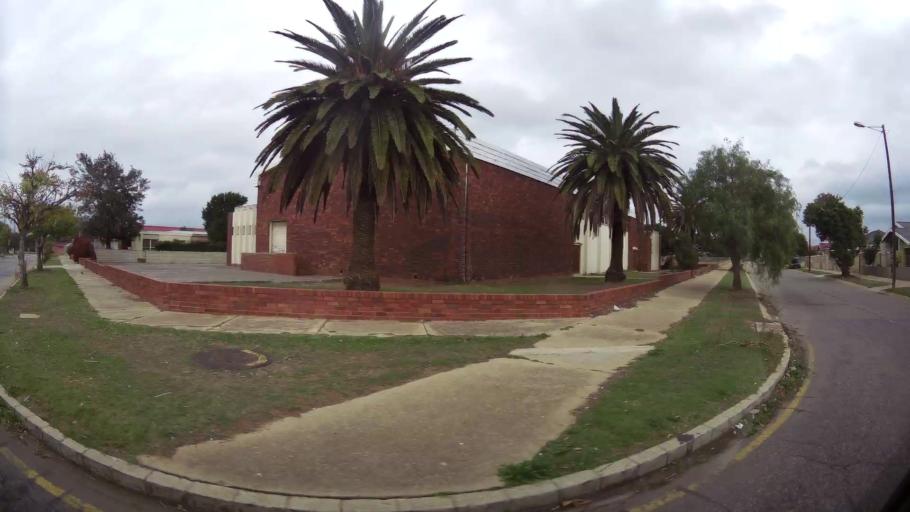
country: ZA
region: Eastern Cape
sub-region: Nelson Mandela Bay Metropolitan Municipality
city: Port Elizabeth
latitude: -33.9003
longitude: 25.5642
